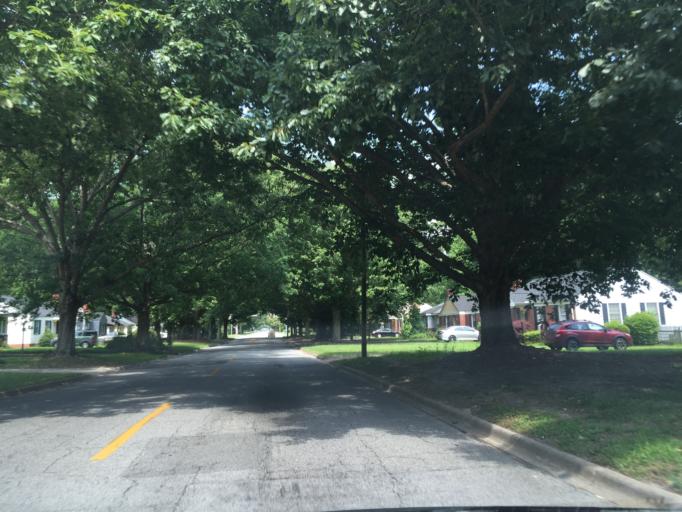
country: US
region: Georgia
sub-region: Chatham County
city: Thunderbolt
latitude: 32.0333
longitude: -81.0976
